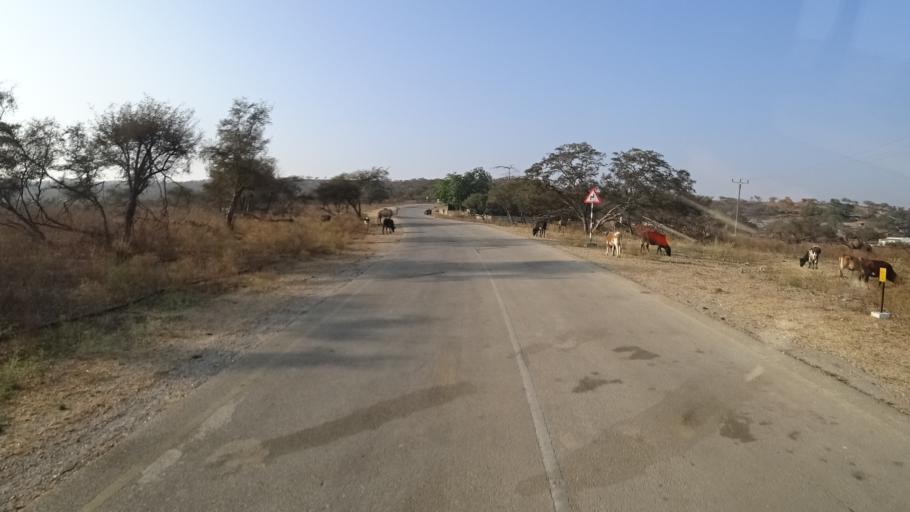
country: YE
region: Al Mahrah
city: Hawf
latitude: 16.7844
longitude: 53.3303
